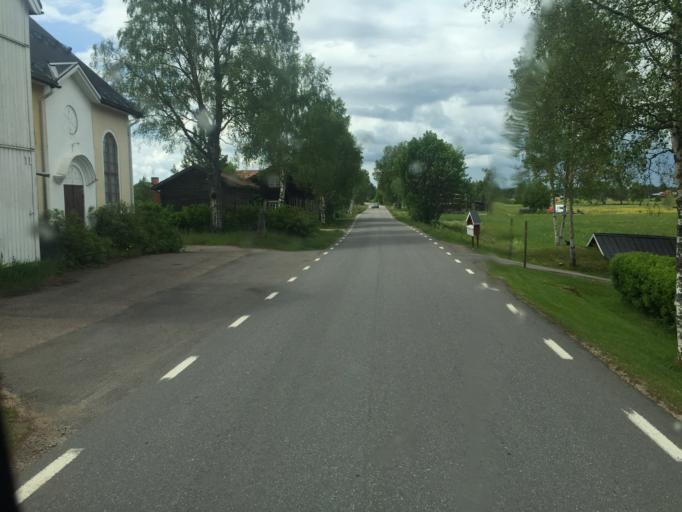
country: SE
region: Dalarna
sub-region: Vansbro Kommun
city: Vansbro
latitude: 60.4592
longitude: 13.9974
